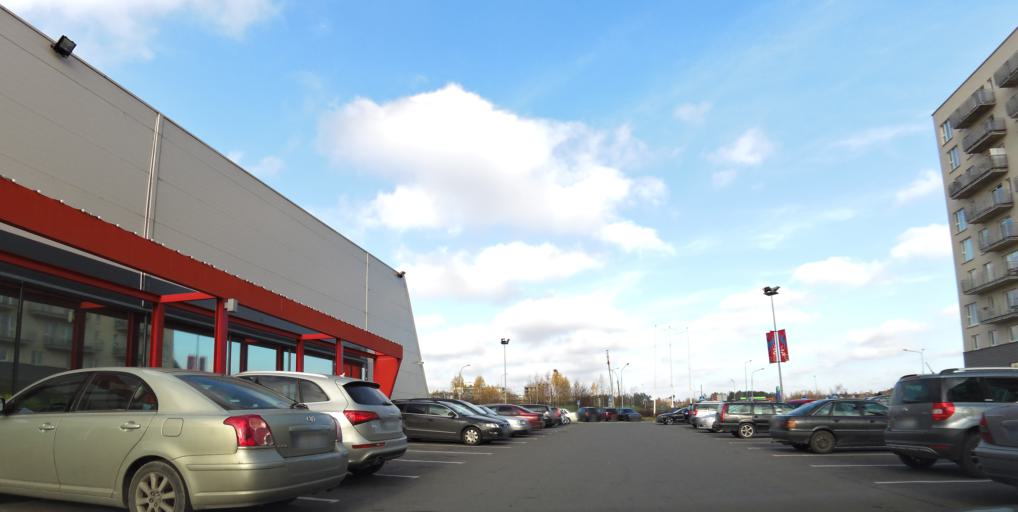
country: LT
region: Vilnius County
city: Pilaite
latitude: 54.7072
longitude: 25.1890
